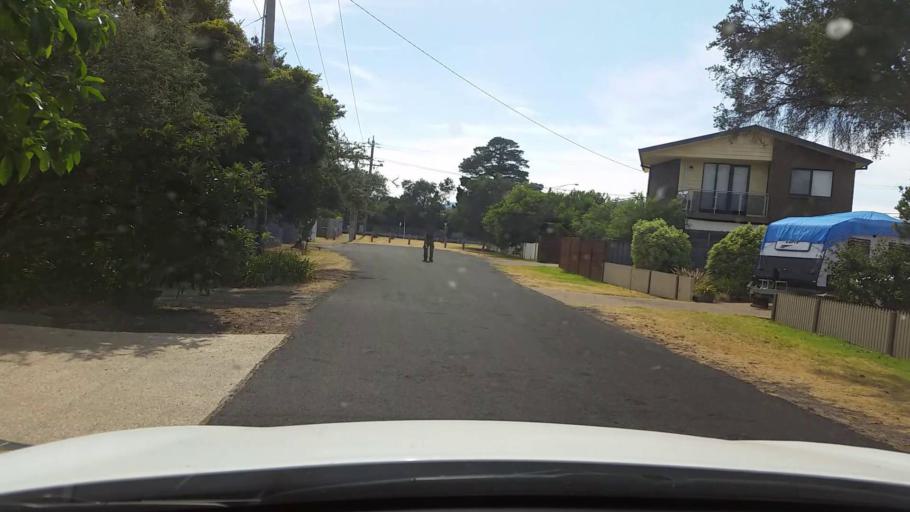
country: AU
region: Victoria
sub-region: Mornington Peninsula
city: Rosebud West
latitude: -38.3670
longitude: 144.8708
